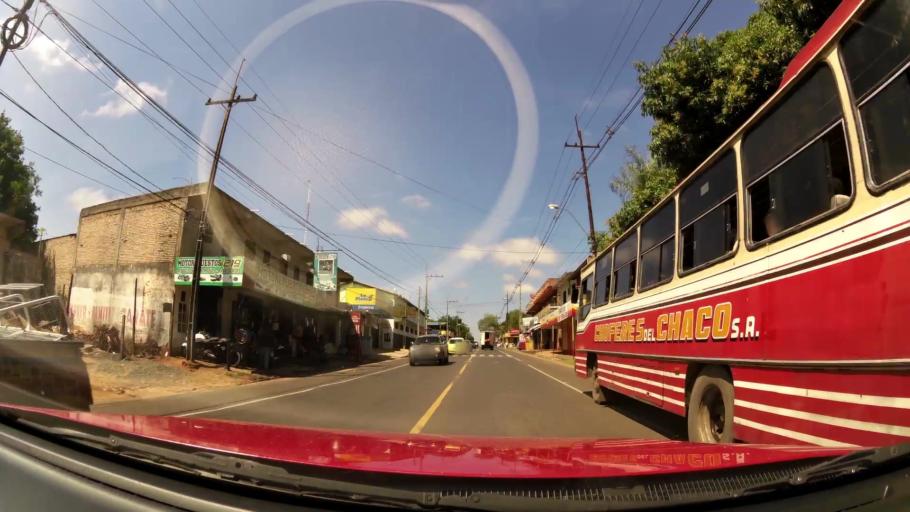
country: PY
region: Central
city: San Lorenzo
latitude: -25.3108
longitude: -57.5061
